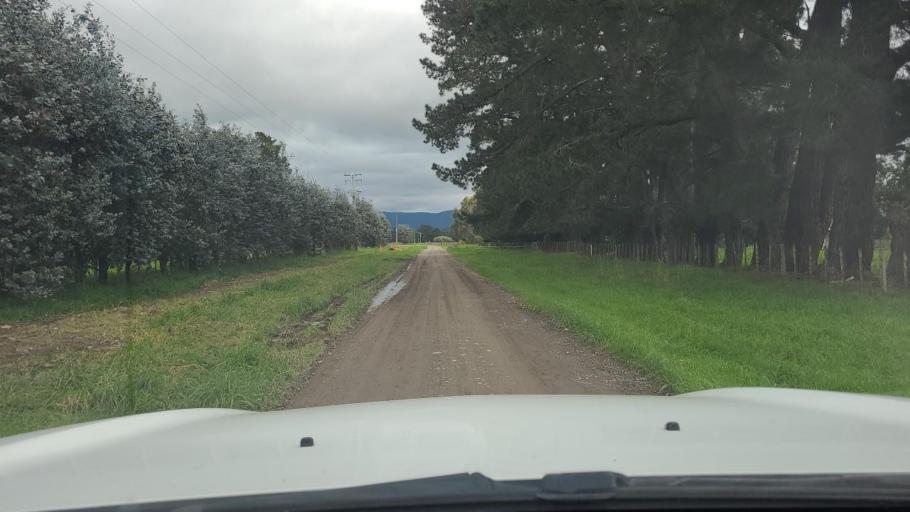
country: NZ
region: Wellington
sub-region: Masterton District
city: Masterton
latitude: -41.1275
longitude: 175.4251
